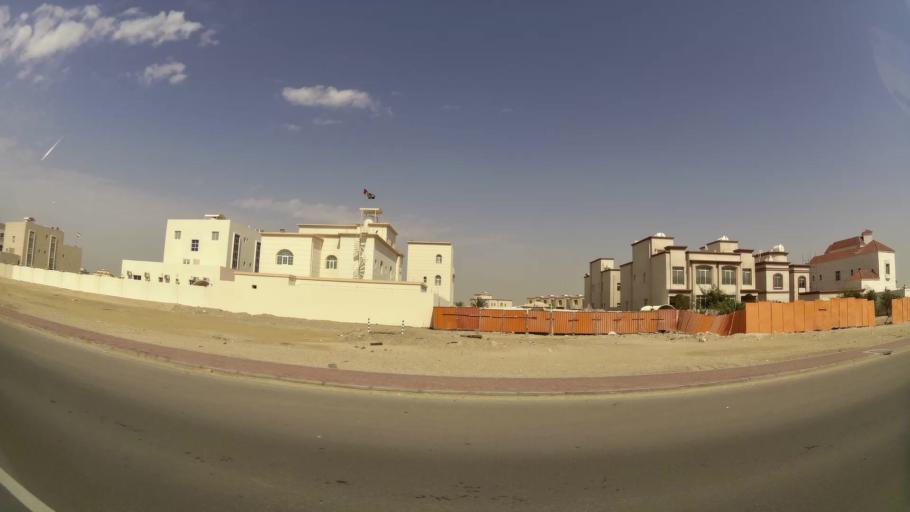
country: AE
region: Abu Dhabi
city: Abu Dhabi
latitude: 24.3123
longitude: 54.5441
